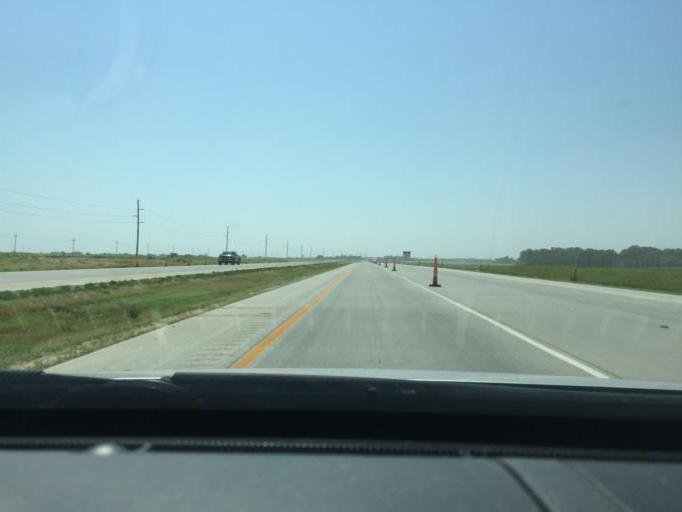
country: US
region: Kansas
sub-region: Reno County
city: South Hutchinson
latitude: 38.0133
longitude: -97.9449
